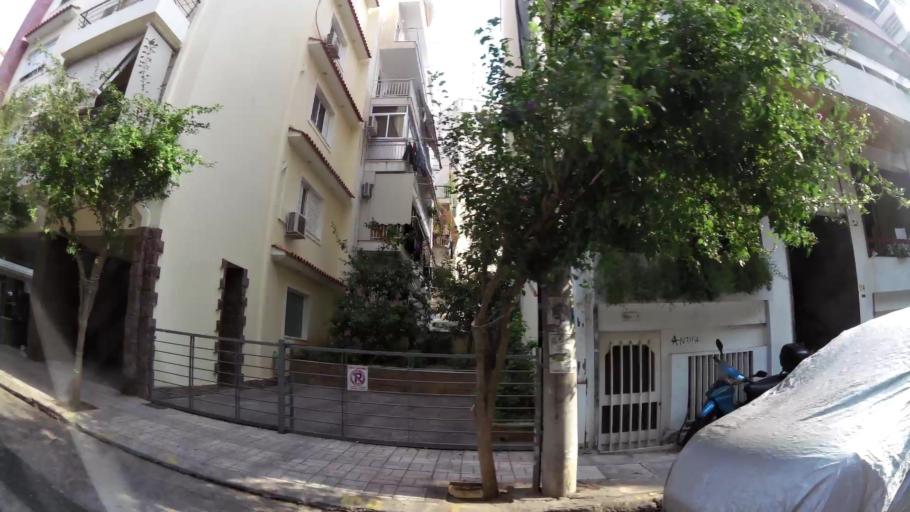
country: GR
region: Attica
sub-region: Nomarchia Athinas
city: Kallithea
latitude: 37.9545
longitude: 23.6950
